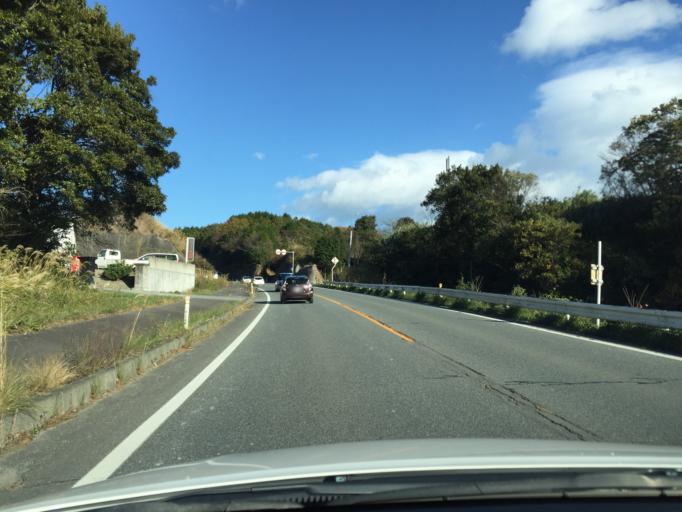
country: JP
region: Fukushima
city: Iwaki
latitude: 37.1919
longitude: 140.9994
